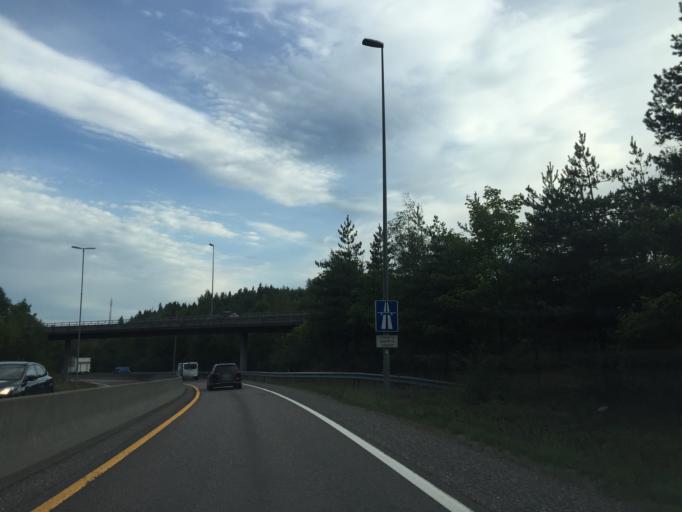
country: NO
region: Akershus
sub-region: Ski
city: Ski
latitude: 59.7393
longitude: 10.7827
